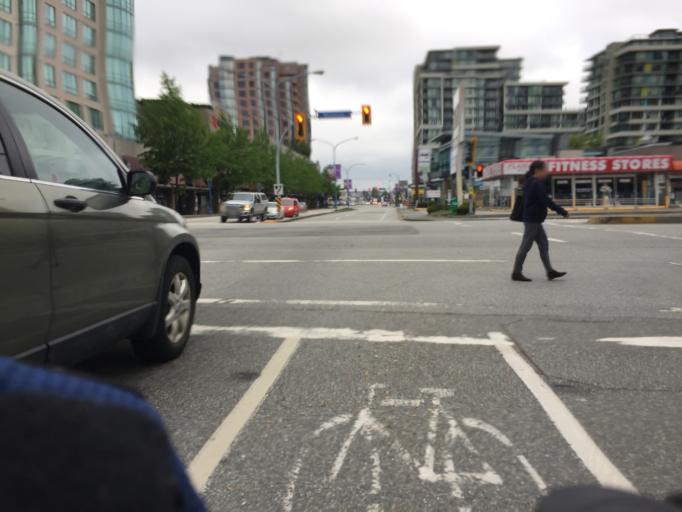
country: CA
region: British Columbia
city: Richmond
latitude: 49.1700
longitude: -123.1402
